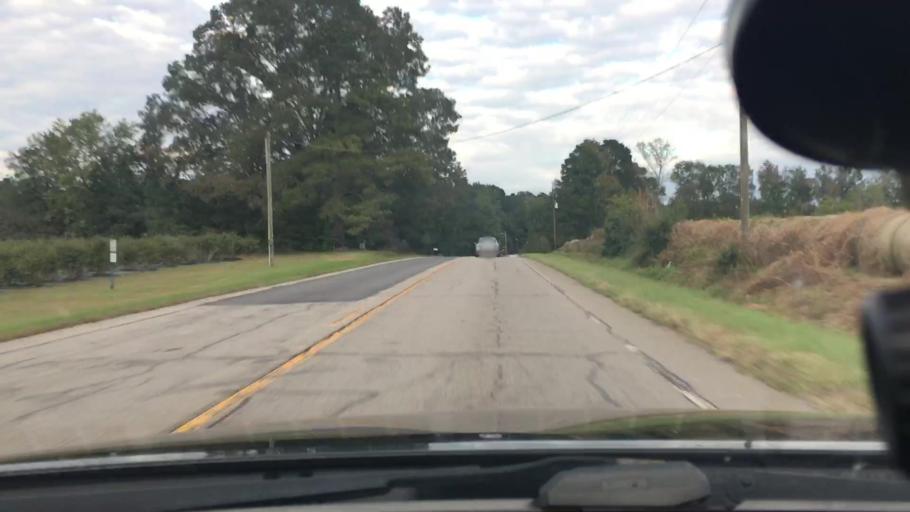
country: US
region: North Carolina
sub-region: Moore County
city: Carthage
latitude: 35.3546
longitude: -79.3462
